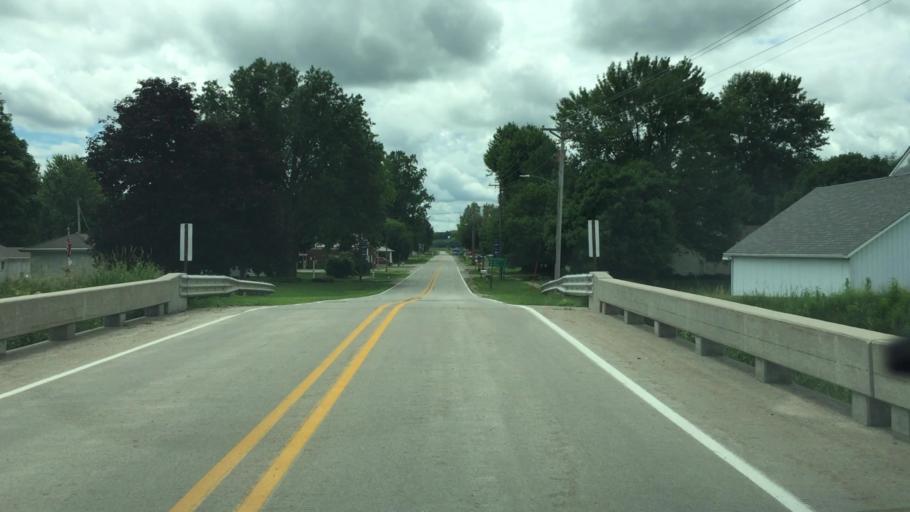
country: US
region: Iowa
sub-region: Jasper County
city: Monroe
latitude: 41.5807
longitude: -93.0235
